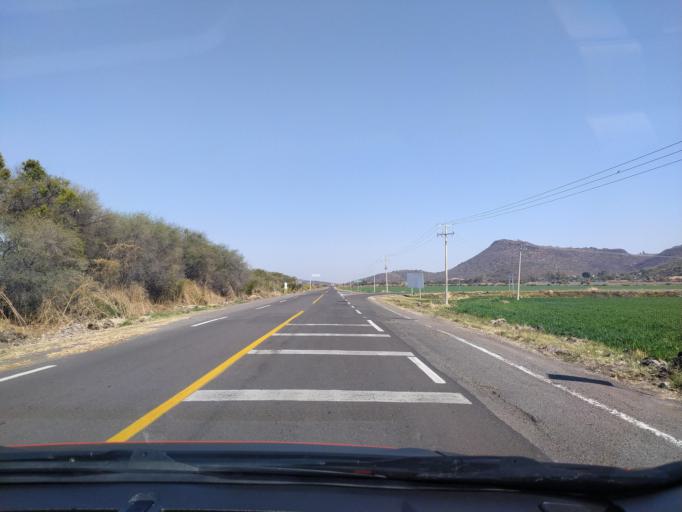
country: MX
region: Guanajuato
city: Ciudad Manuel Doblado
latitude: 20.7791
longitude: -101.8330
